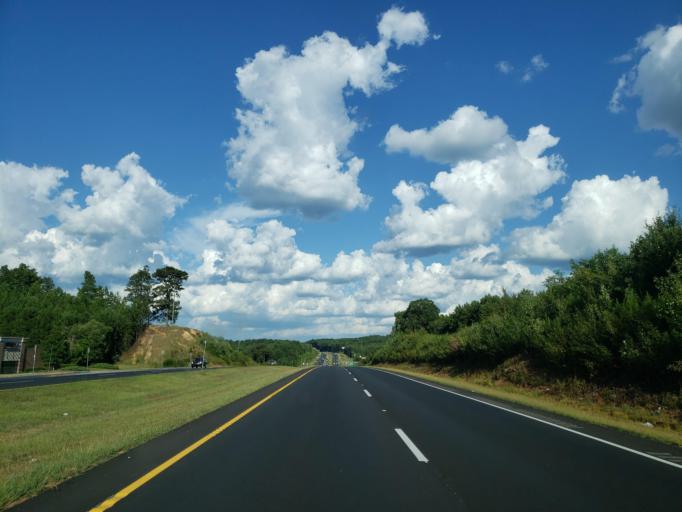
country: US
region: Georgia
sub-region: Floyd County
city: Rome
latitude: 34.2189
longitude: -85.1304
